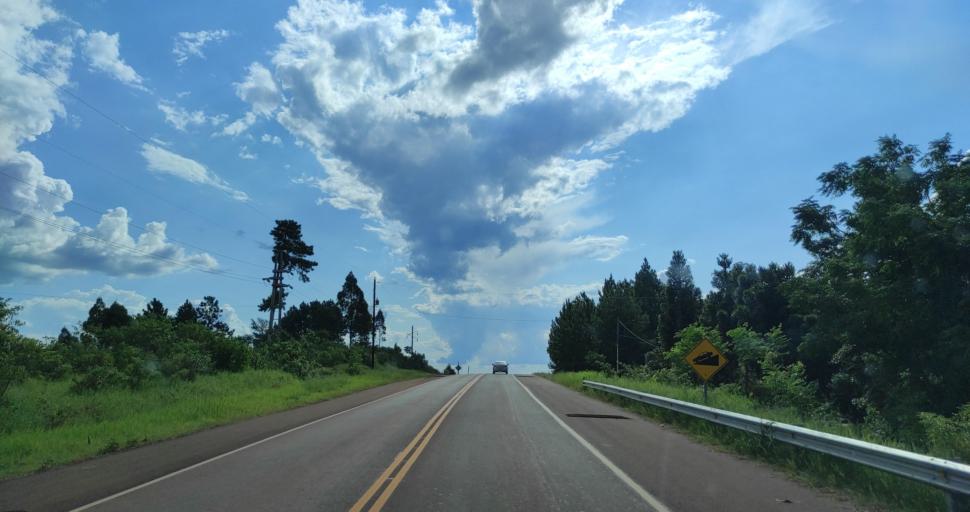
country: AR
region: Misiones
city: Bernardo de Irigoyen
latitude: -26.2948
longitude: -53.7792
